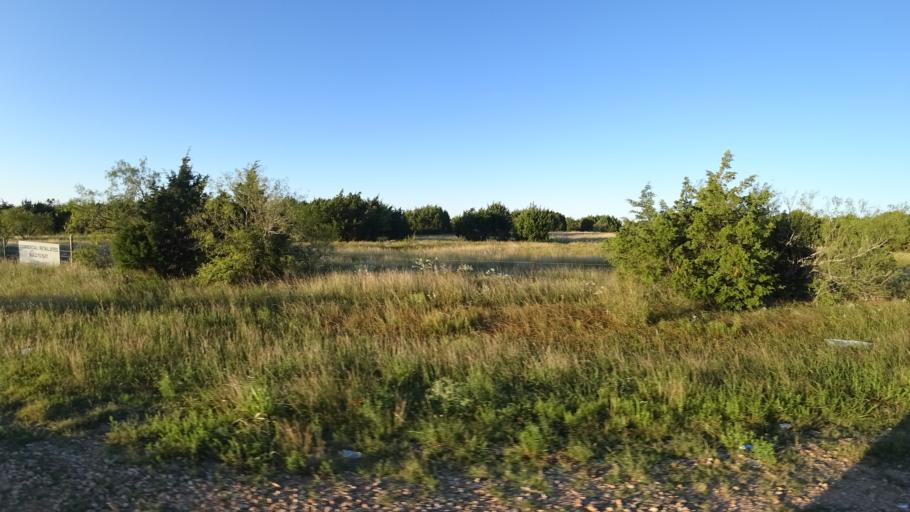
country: US
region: Texas
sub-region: Travis County
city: Hornsby Bend
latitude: 30.2885
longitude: -97.6243
